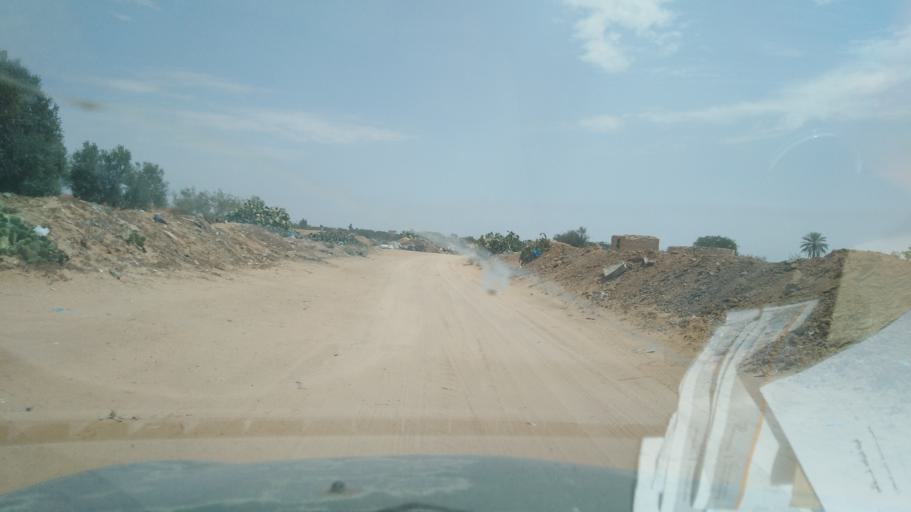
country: TN
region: Safaqis
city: Sfax
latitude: 34.7388
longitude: 10.5451
